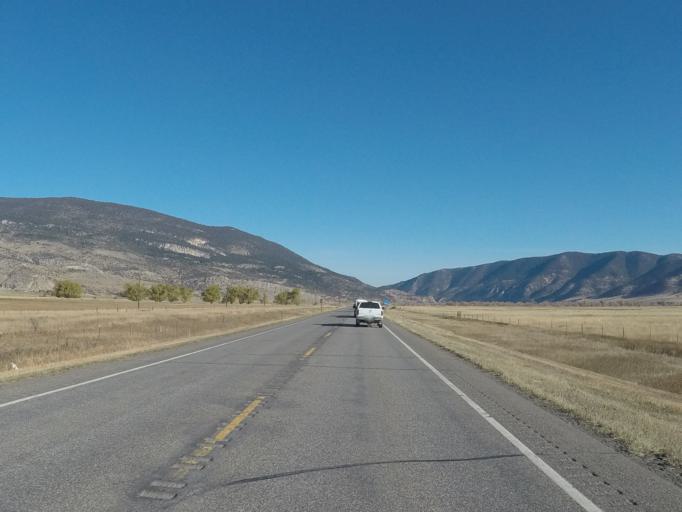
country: US
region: Montana
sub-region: Park County
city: Livingston
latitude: 45.5466
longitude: -110.5989
